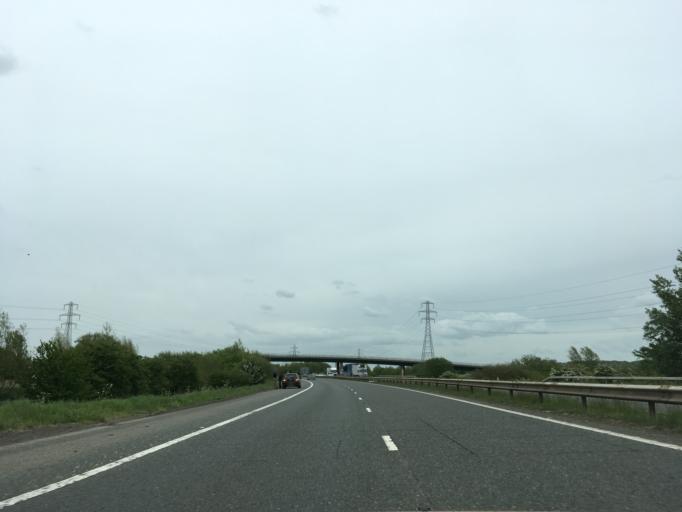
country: GB
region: England
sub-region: South Gloucestershire
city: Severn Beach
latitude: 51.5114
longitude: -2.6646
